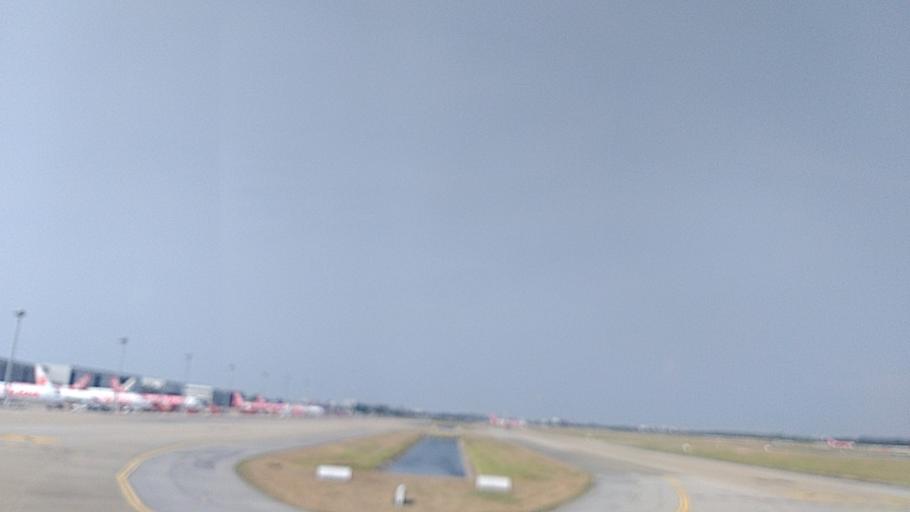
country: TH
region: Bangkok
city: Don Mueang
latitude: 13.9209
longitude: 100.6070
